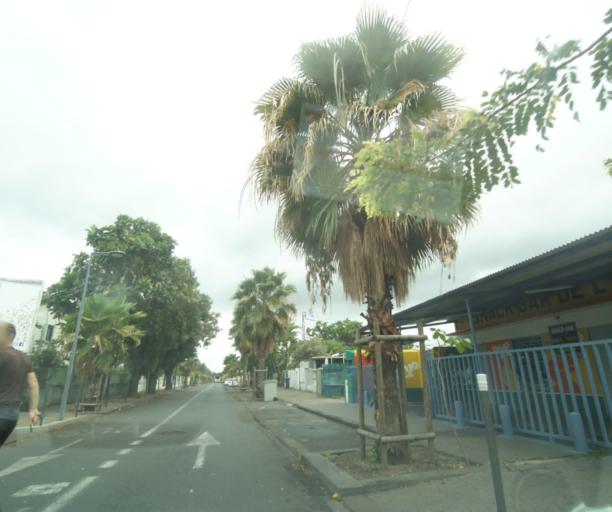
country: RE
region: Reunion
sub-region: Reunion
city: Saint-Paul
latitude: -20.9944
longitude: 55.2846
